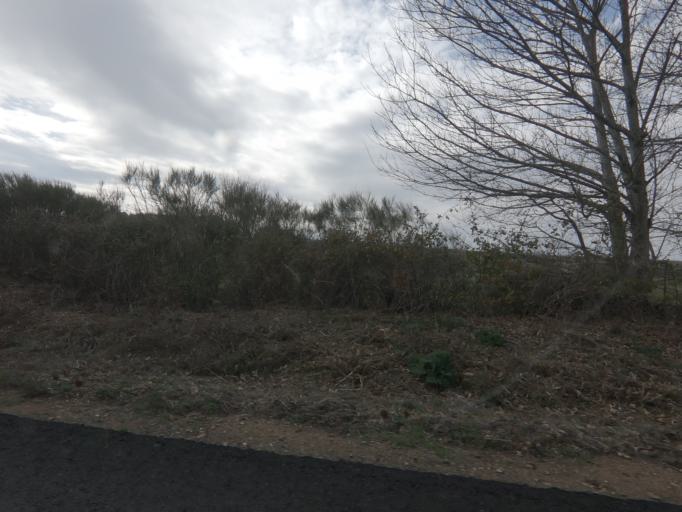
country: ES
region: Castille and Leon
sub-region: Provincia de Salamanca
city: Villasrubias
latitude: 40.3502
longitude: -6.6327
